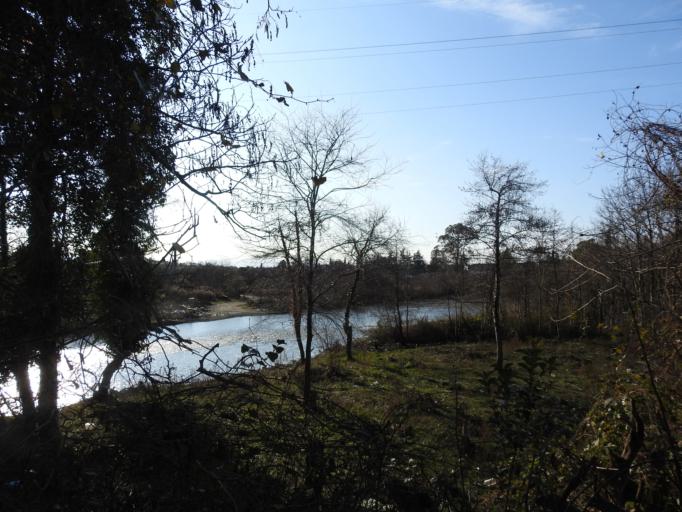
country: GE
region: Abkhazia
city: Gulrip'shi
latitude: 42.9528
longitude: 41.0910
